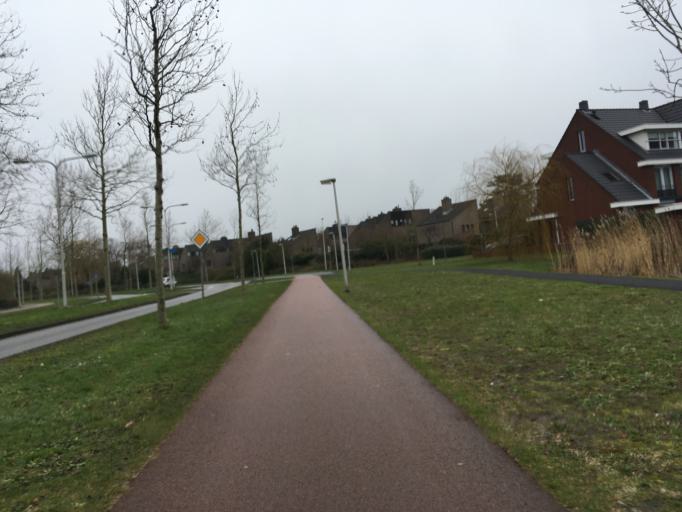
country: NL
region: North Holland
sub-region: Gemeente Heemstede
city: Heemstede
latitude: 52.3550
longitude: 4.6319
